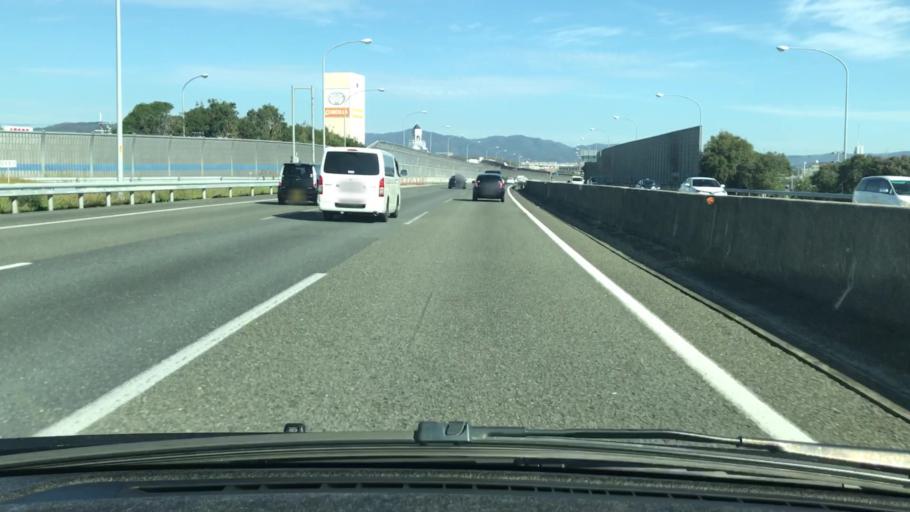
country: JP
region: Osaka
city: Ibaraki
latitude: 34.8302
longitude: 135.5589
